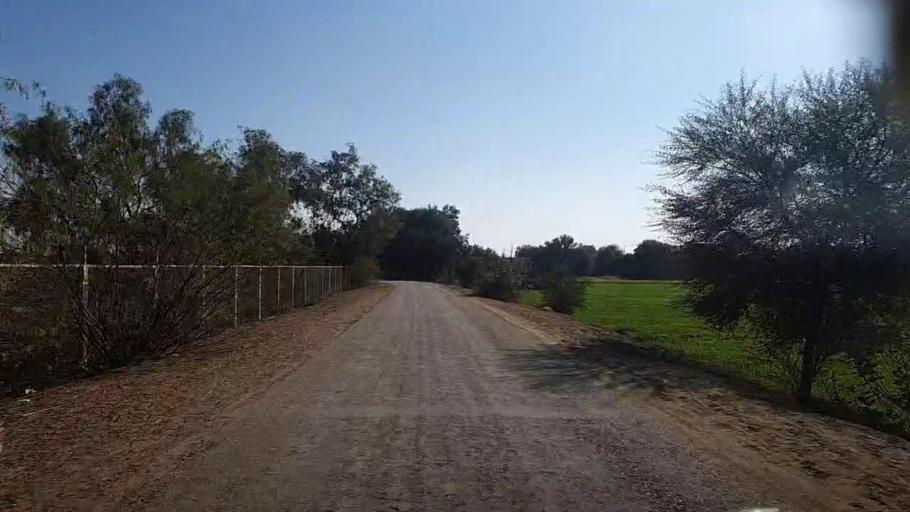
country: PK
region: Sindh
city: Khairpur
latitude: 27.9133
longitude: 69.7512
